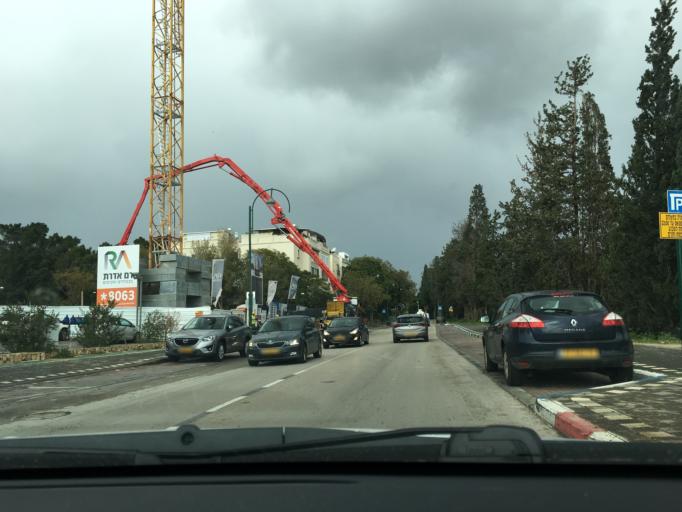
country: IL
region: Tel Aviv
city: Ramat HaSharon
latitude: 32.1414
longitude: 34.8465
